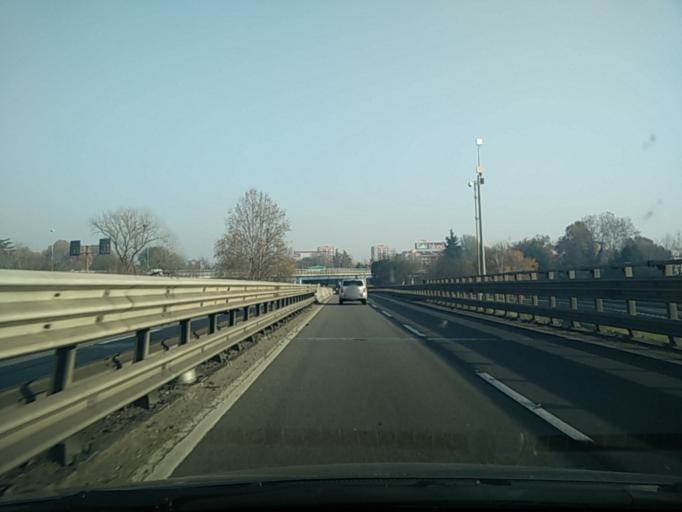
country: IT
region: Lombardy
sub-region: Citta metropolitana di Milano
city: Baranzate
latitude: 45.5155
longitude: 9.1183
